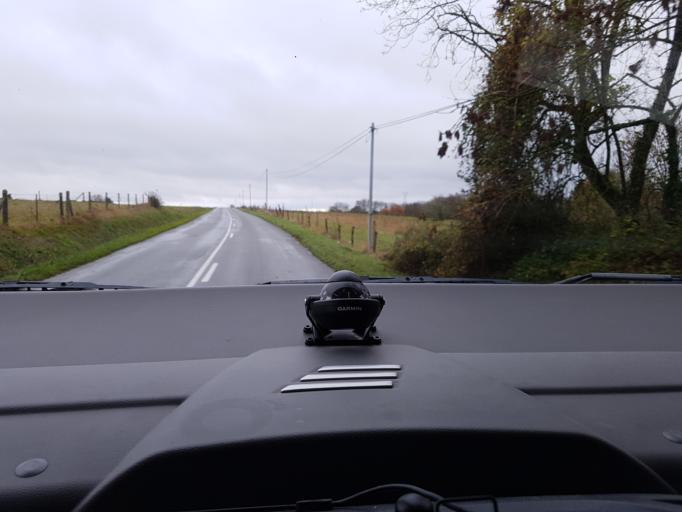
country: FR
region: Haute-Normandie
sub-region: Departement de l'Eure
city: Pont-Saint-Pierre
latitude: 49.3110
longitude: 1.3114
